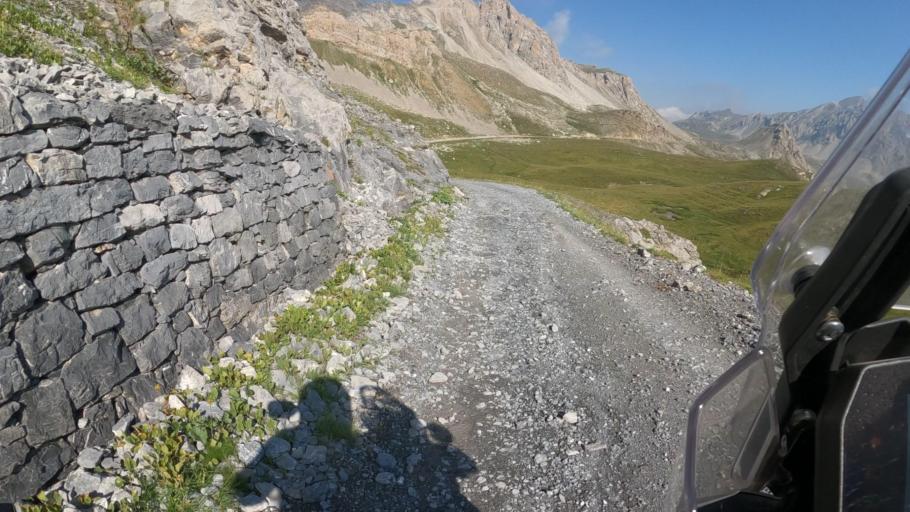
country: IT
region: Piedmont
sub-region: Provincia di Cuneo
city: Pietraporzio
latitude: 44.3860
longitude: 7.0327
